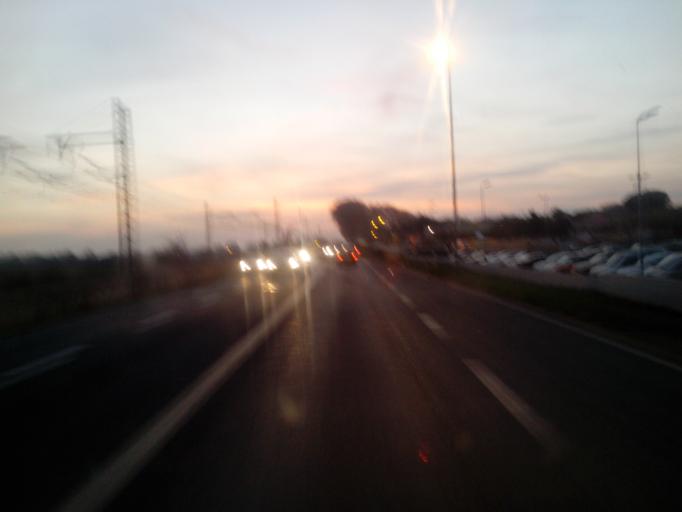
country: FR
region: Languedoc-Roussillon
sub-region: Departement de l'Herault
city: Saint-Bres
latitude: 43.6649
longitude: 4.0383
